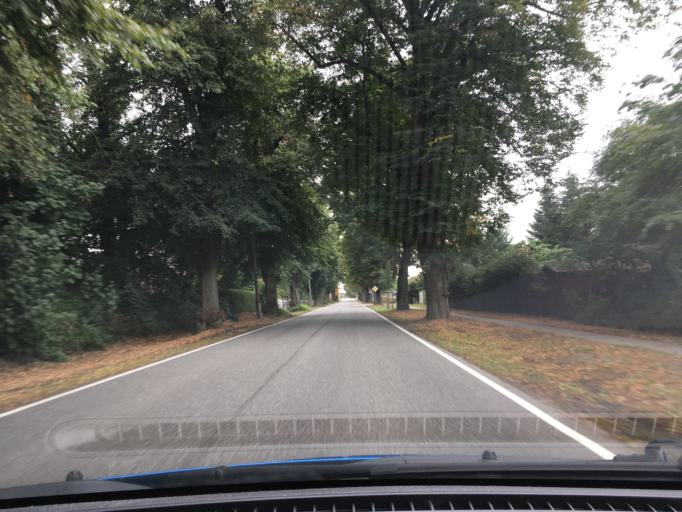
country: DE
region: Mecklenburg-Vorpommern
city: Wittenburg
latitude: 53.5041
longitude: 11.0775
